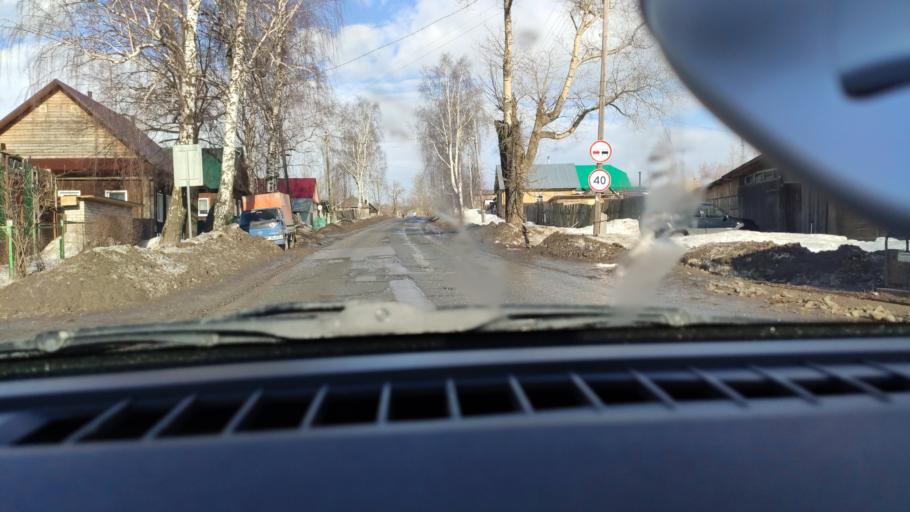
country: RU
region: Perm
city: Nytva
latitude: 57.9472
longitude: 55.3477
